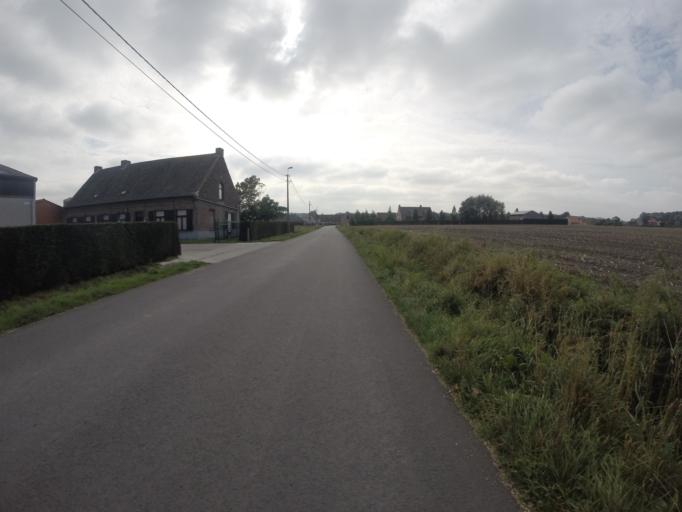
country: BE
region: Flanders
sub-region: Provincie Oost-Vlaanderen
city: Aalter
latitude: 51.0759
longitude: 3.4257
